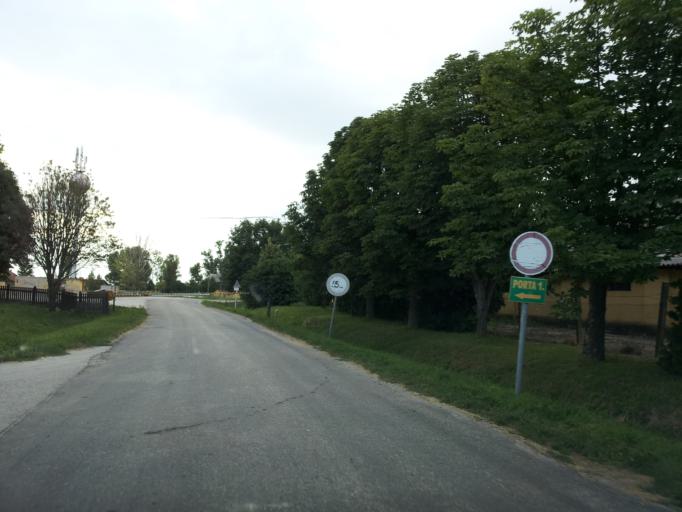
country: HU
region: Somogy
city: Balatonszabadi
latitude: 46.8968
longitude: 18.1369
